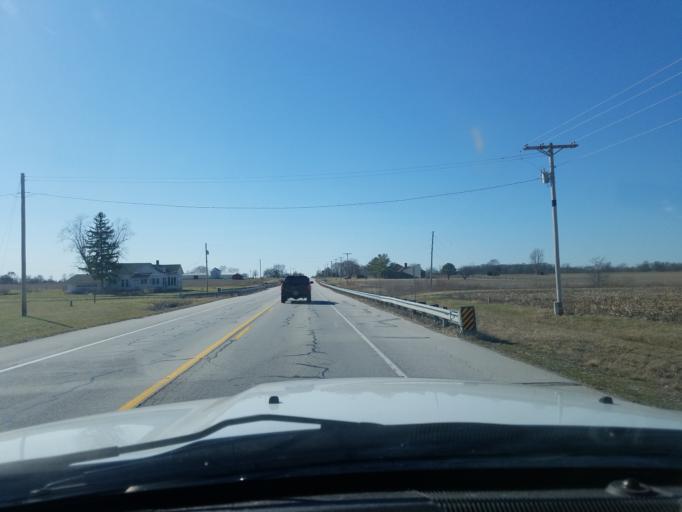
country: US
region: Indiana
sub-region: Shelby County
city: Shelbyville
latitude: 39.4960
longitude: -85.8892
